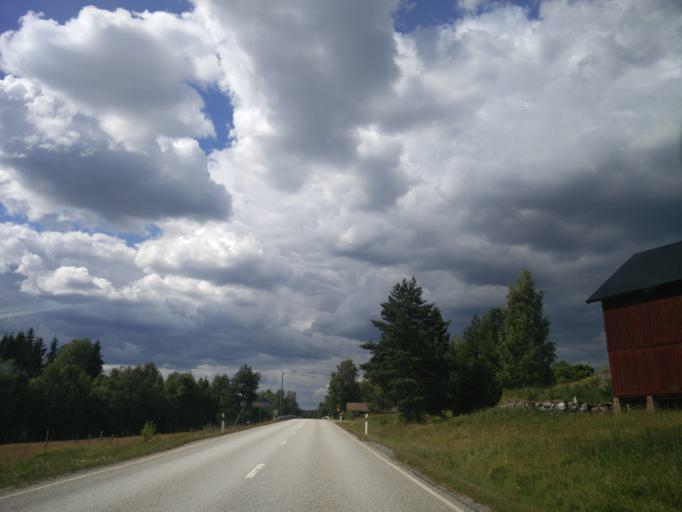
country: SE
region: OErebro
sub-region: Ljusnarsbergs Kommun
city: Kopparberg
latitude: 59.7841
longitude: 14.7761
